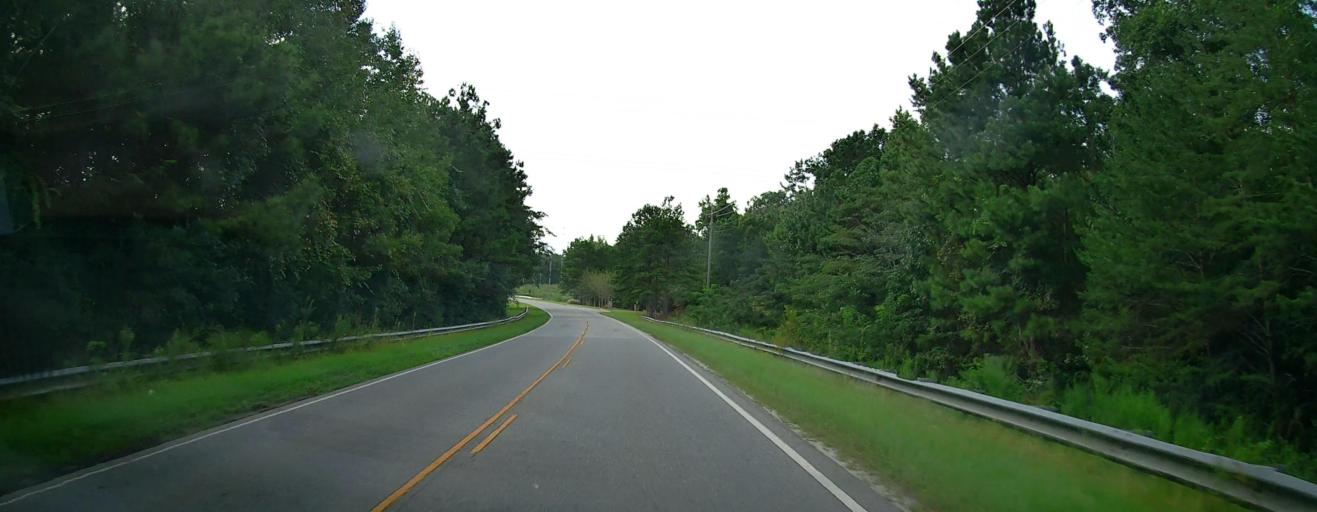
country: US
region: Alabama
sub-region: Russell County
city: Phenix City
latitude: 32.5154
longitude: -85.0117
